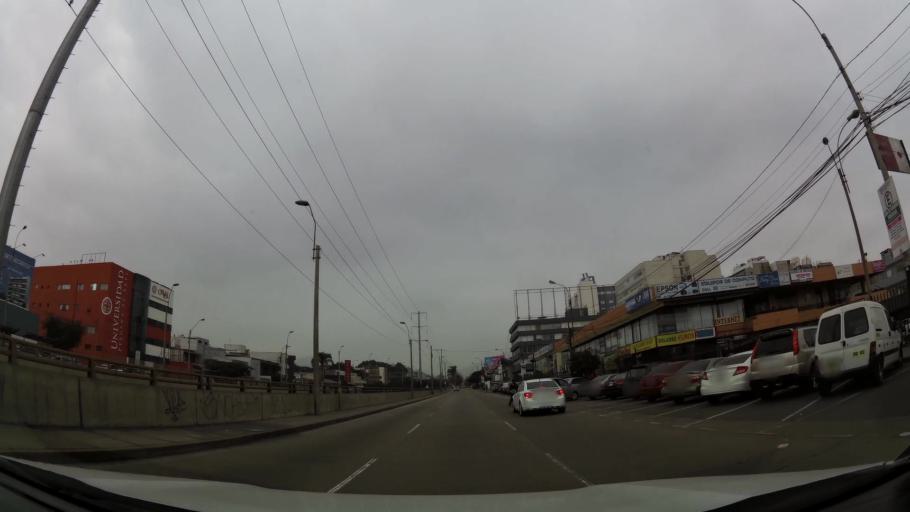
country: PE
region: Lima
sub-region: Lima
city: Surco
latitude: -12.1113
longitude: -76.9917
